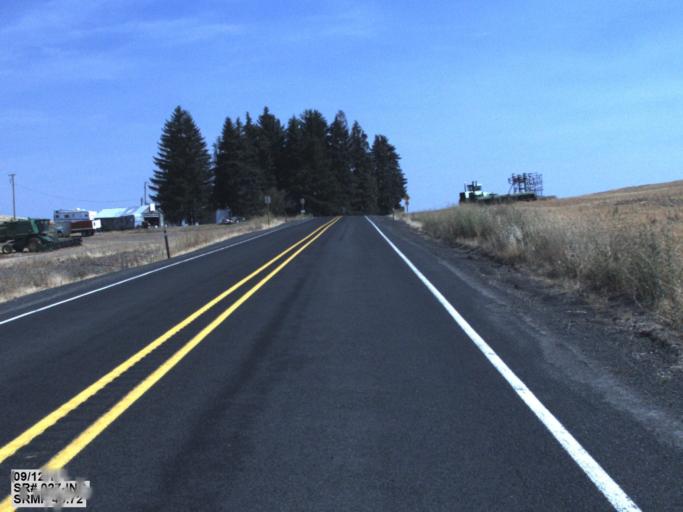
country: US
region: Idaho
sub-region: Benewah County
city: Plummer
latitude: 47.1951
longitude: -117.1012
